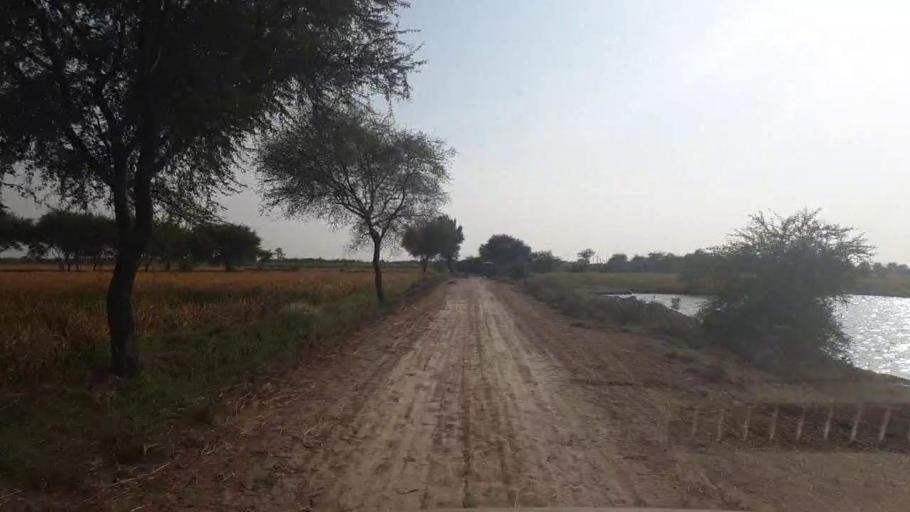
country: PK
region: Sindh
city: Badin
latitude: 24.6355
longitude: 68.7986
